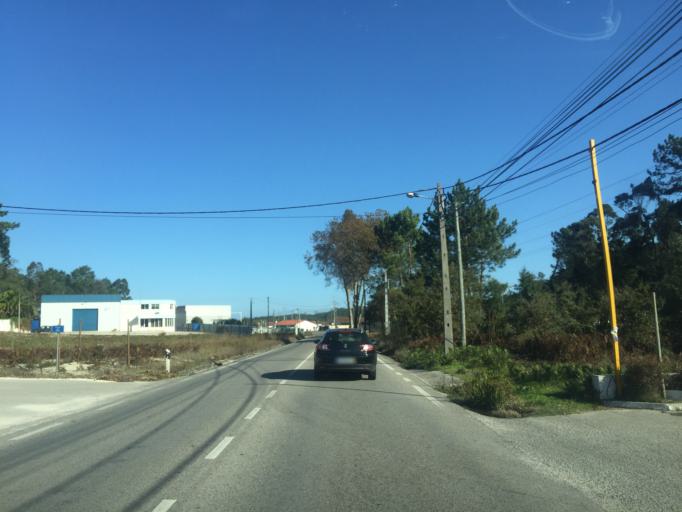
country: PT
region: Leiria
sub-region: Leiria
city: Amor
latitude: 39.8214
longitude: -8.8400
